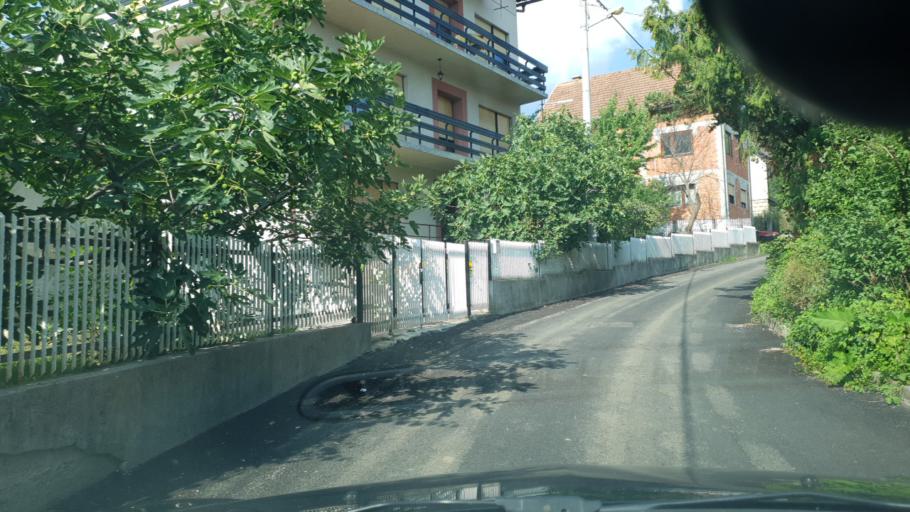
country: HR
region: Grad Zagreb
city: Stenjevec
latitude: 45.8343
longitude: 15.9032
